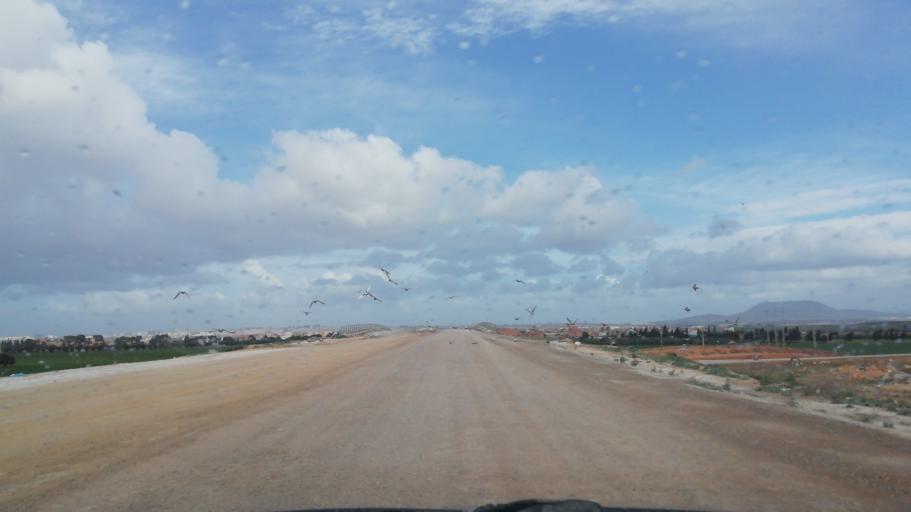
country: DZ
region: Oran
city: Sidi ech Chahmi
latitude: 35.6471
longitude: -0.5173
